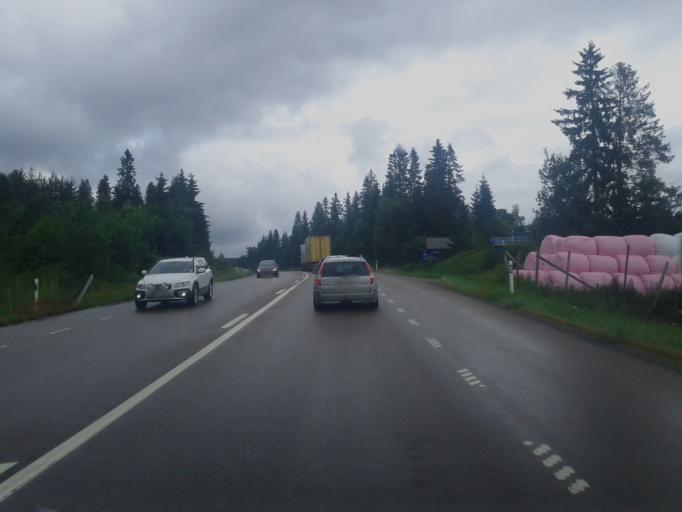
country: SE
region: Vaesternorrland
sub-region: Haernoesands Kommun
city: Haernoesand
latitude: 62.6898
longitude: 17.8506
